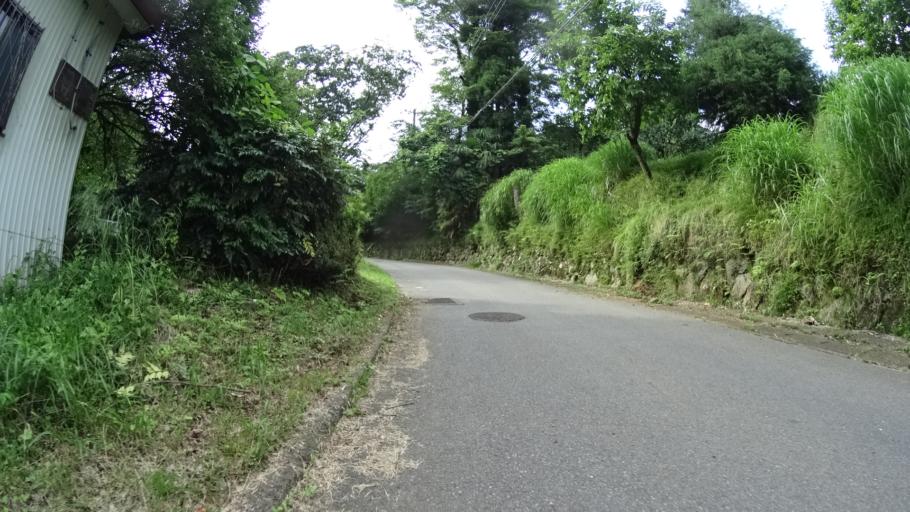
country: JP
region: Kanagawa
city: Atsugi
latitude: 35.4970
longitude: 139.2681
